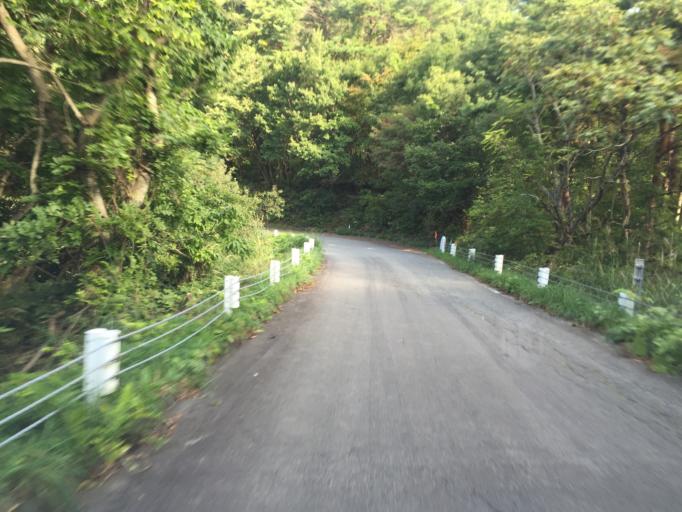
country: JP
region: Fukushima
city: Inawashiro
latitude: 37.4883
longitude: 139.9702
